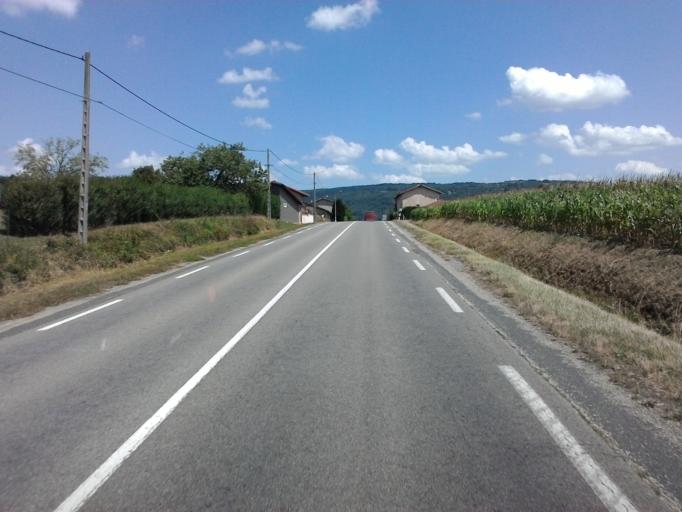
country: FR
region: Rhone-Alpes
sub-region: Departement de l'Ain
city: Coligny
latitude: 46.3636
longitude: 5.3317
